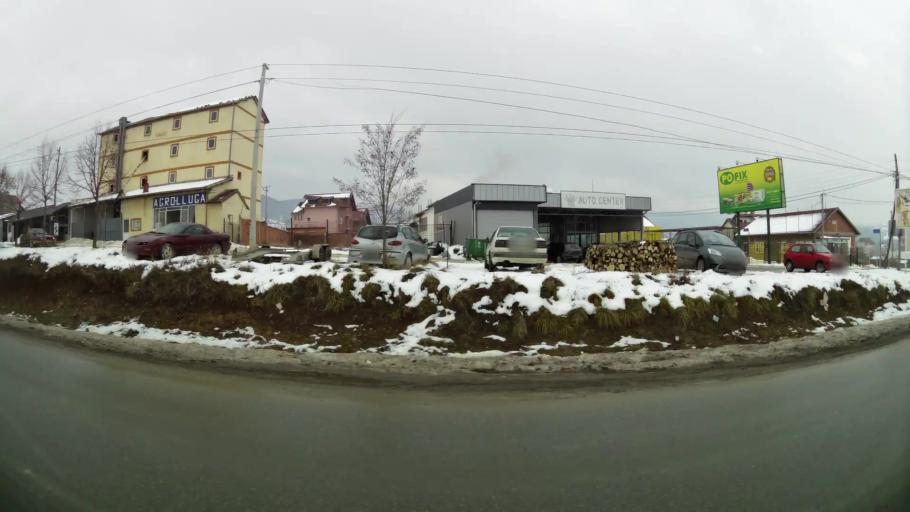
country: XK
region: Pristina
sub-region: Komuna e Prishtines
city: Pristina
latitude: 42.7130
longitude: 21.1511
